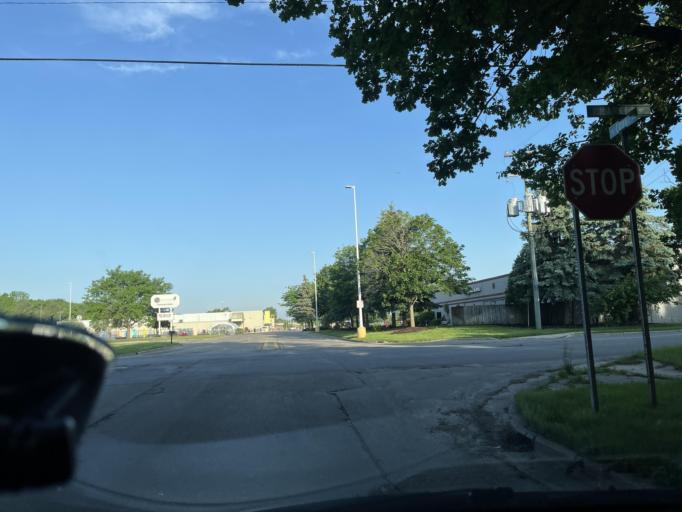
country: US
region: Michigan
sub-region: Barry County
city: Hastings
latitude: 42.6478
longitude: -85.2949
